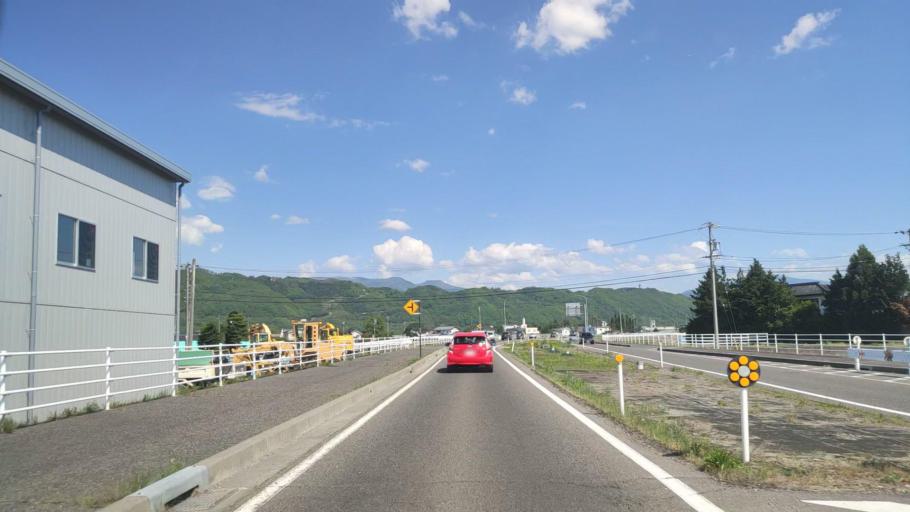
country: JP
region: Nagano
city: Toyoshina
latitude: 36.2794
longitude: 137.9219
